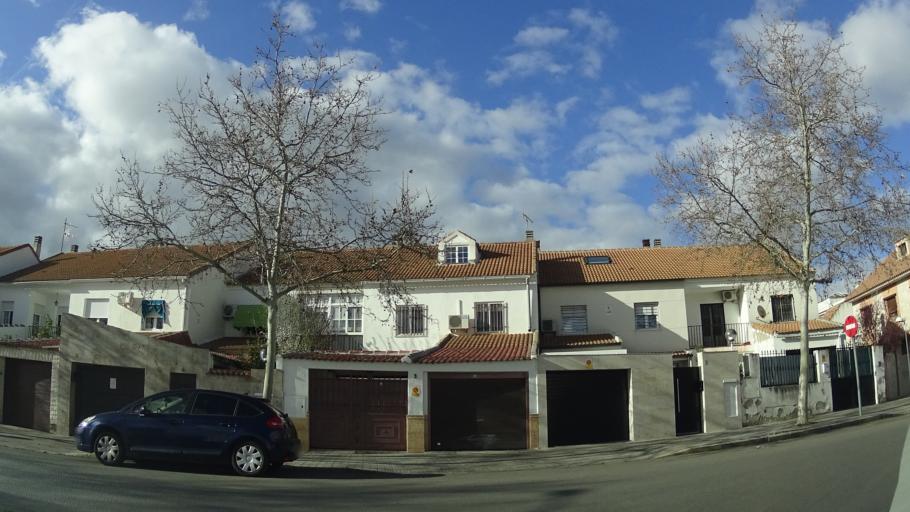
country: ES
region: Castille-La Mancha
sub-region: Provincia de Ciudad Real
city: Ciudad Real
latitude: 38.9778
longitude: -3.9306
